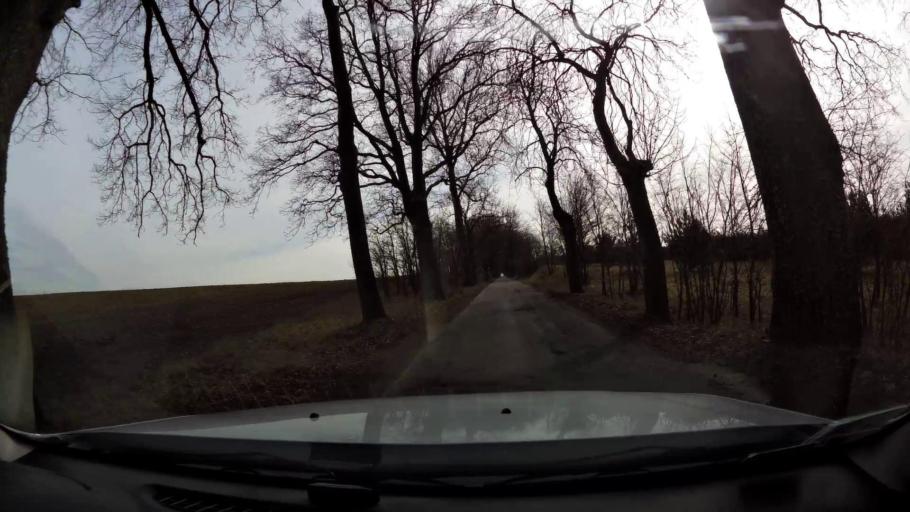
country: PL
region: West Pomeranian Voivodeship
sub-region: Powiat stargardzki
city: Insko
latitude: 53.4522
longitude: 15.6359
